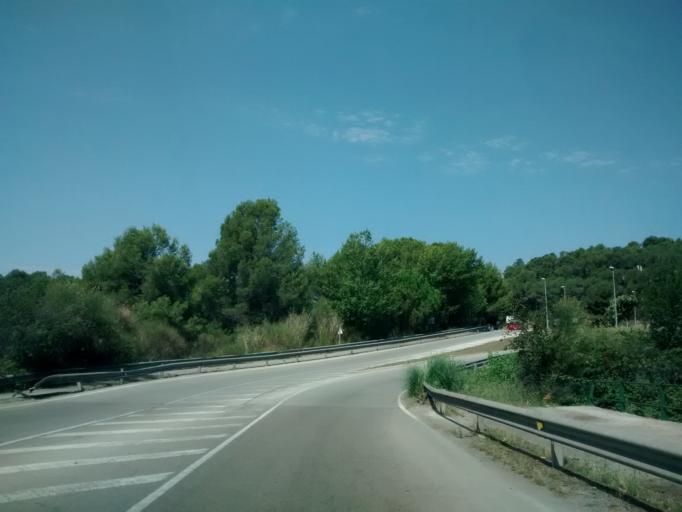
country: ES
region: Catalonia
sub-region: Provincia de Barcelona
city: Sant Quirze del Valles
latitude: 41.5086
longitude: 2.0931
